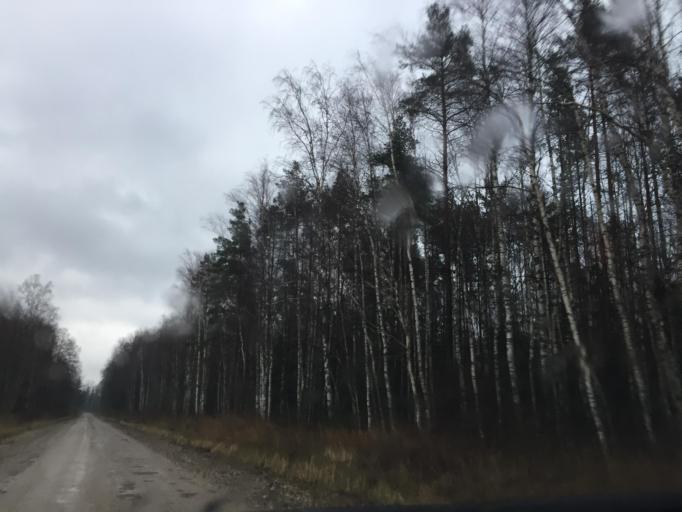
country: LV
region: Aloja
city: Staicele
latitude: 57.7535
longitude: 24.6039
